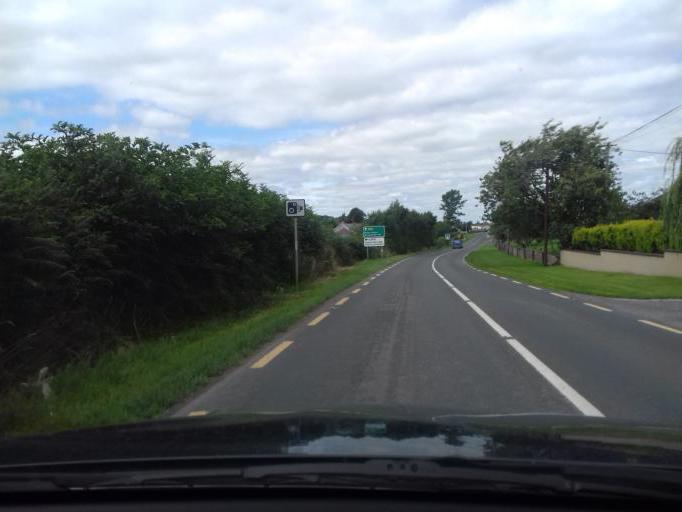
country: IE
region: Leinster
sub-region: Wicklow
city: Baltinglass
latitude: 52.9290
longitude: -6.7101
